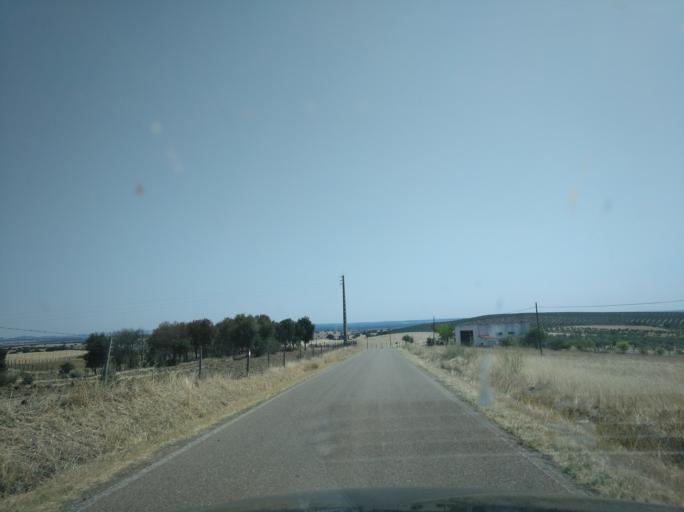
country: PT
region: Portalegre
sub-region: Campo Maior
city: Campo Maior
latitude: 39.0259
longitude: -7.0305
